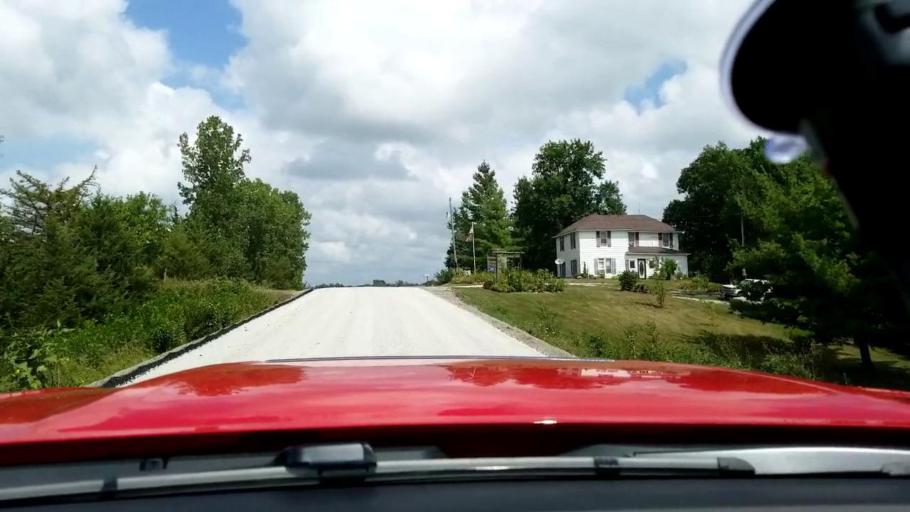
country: US
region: Iowa
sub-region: Decatur County
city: Lamoni
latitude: 40.6453
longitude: -94.0531
